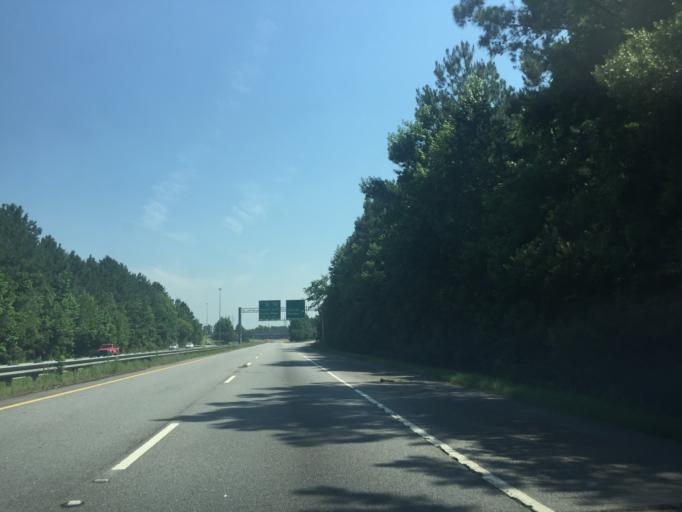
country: US
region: Georgia
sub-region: Chatham County
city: Georgetown
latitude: 32.0344
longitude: -81.1662
